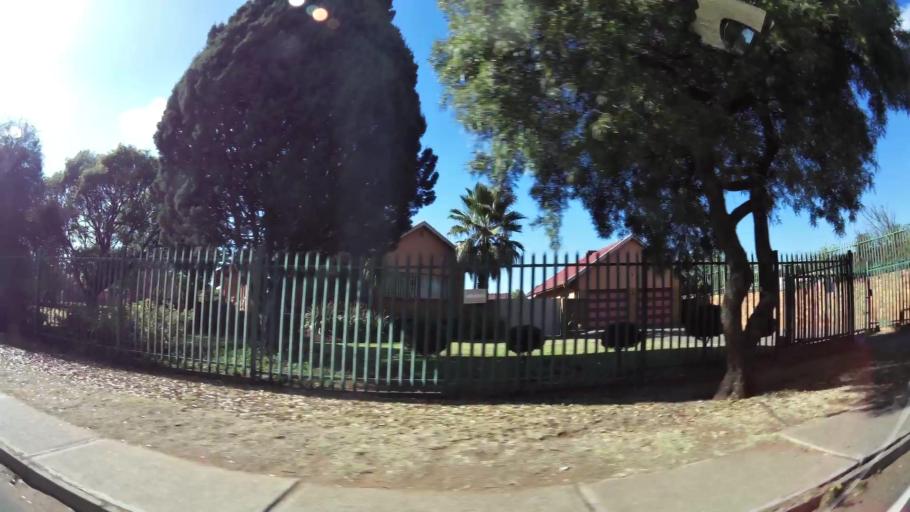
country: ZA
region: Gauteng
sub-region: City of Johannesburg Metropolitan Municipality
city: Roodepoort
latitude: -26.1390
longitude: 27.8327
